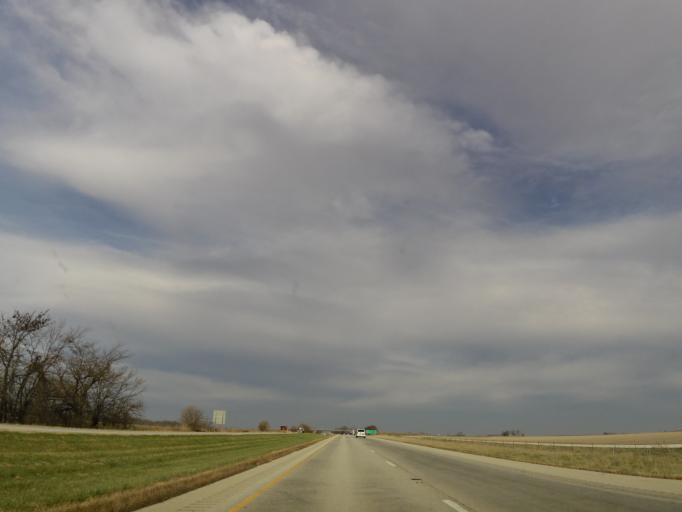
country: US
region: Illinois
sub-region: Knox County
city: Galesburg
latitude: 41.0000
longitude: -90.3353
